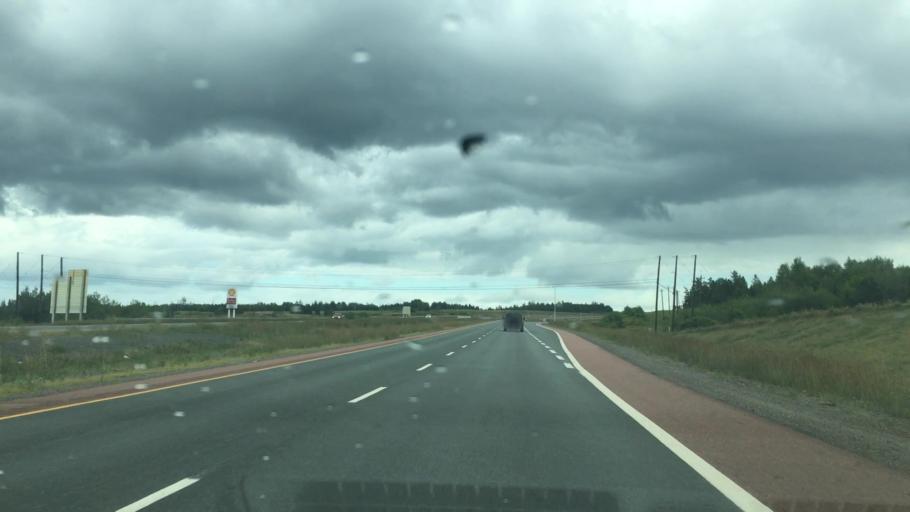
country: CA
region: Nova Scotia
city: Antigonish
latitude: 45.6092
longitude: -61.9759
